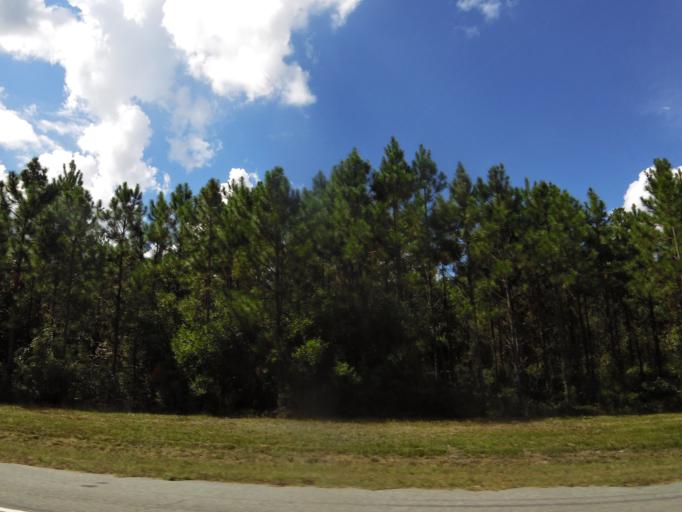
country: US
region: Georgia
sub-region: Charlton County
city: Folkston
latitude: 30.9848
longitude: -82.0256
